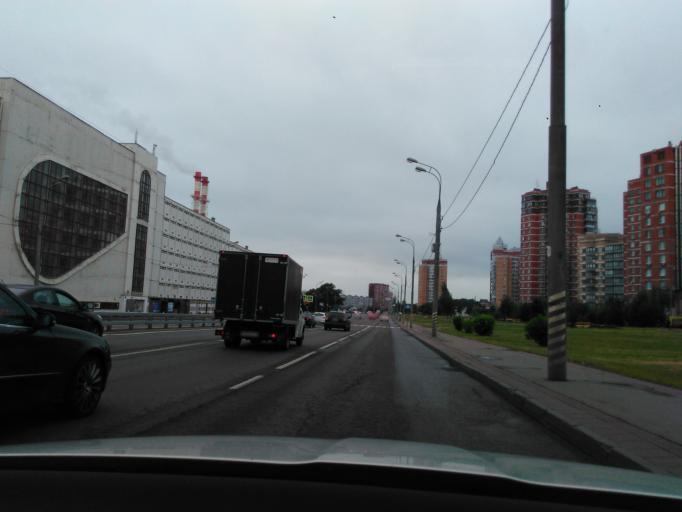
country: RU
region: Moscow
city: Khimki
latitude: 55.8971
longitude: 37.4001
